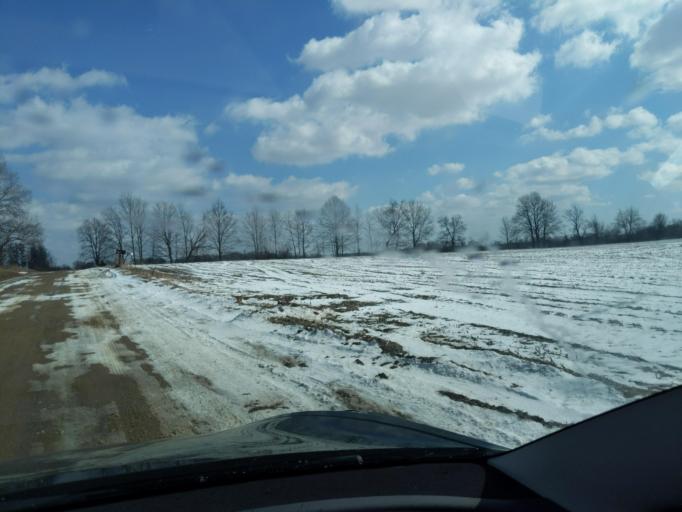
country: US
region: Michigan
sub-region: Livingston County
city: Fowlerville
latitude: 42.6140
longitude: -84.1070
